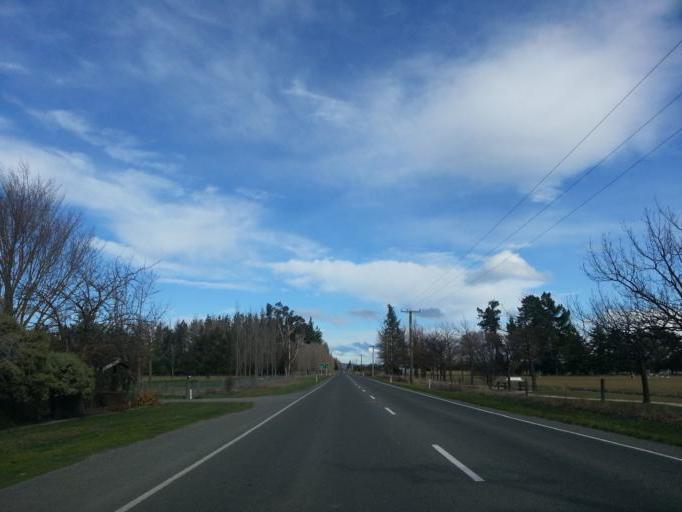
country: NZ
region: Canterbury
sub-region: Hurunui District
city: Amberley
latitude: -42.7766
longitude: 172.8461
